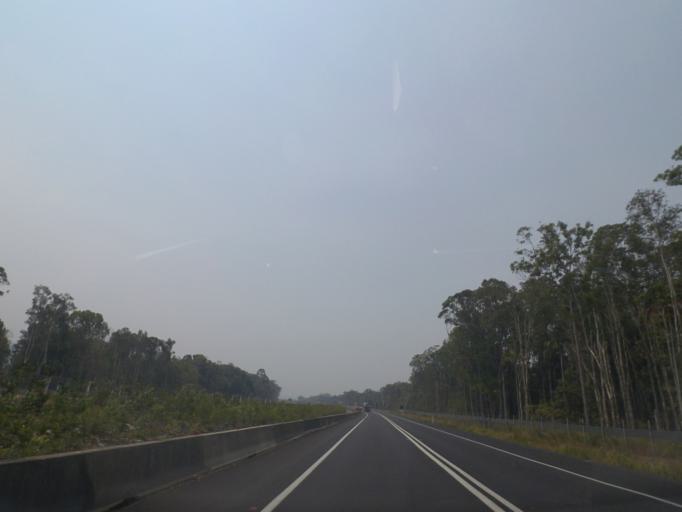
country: AU
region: New South Wales
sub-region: Ballina
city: Ballina
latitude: -28.9155
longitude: 153.4776
